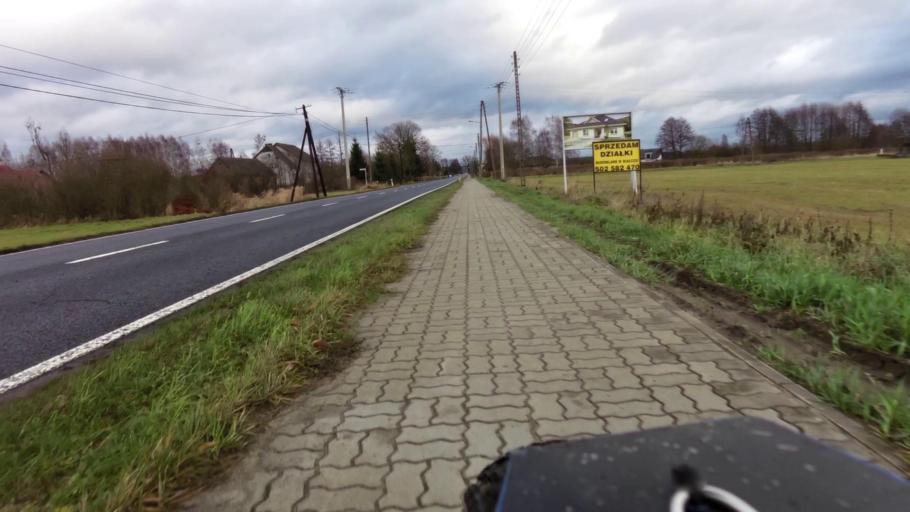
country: PL
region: Lubusz
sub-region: Powiat gorzowski
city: Witnica
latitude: 52.6754
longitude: 14.9296
